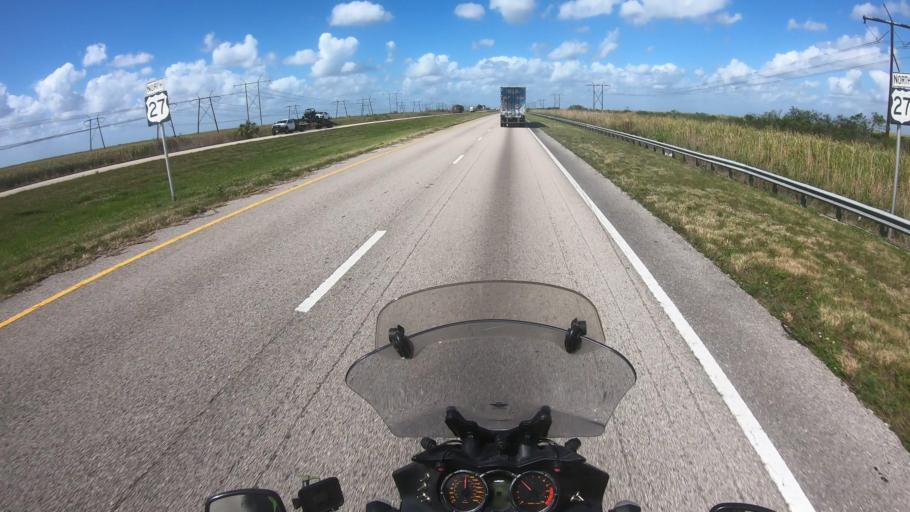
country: US
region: Florida
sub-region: Broward County
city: Weston
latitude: 26.1973
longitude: -80.4529
